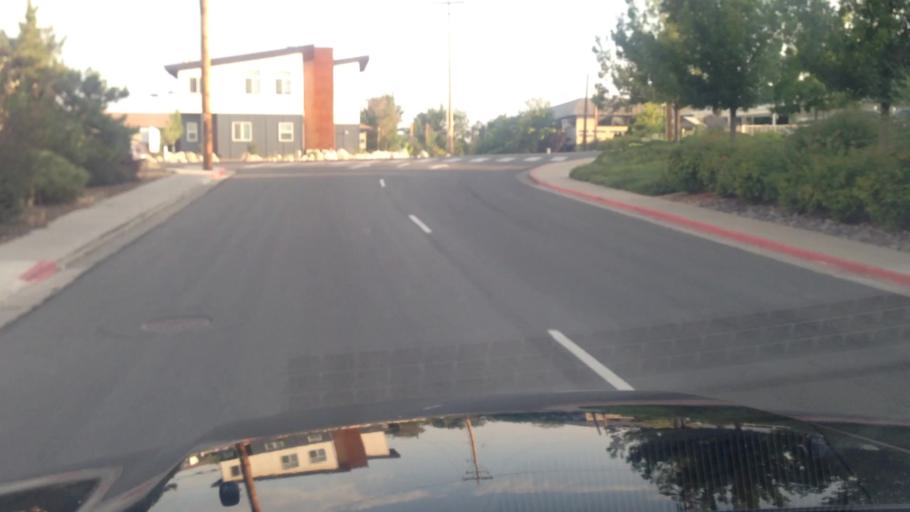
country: US
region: Nevada
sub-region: Washoe County
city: Reno
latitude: 39.5228
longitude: -119.7983
